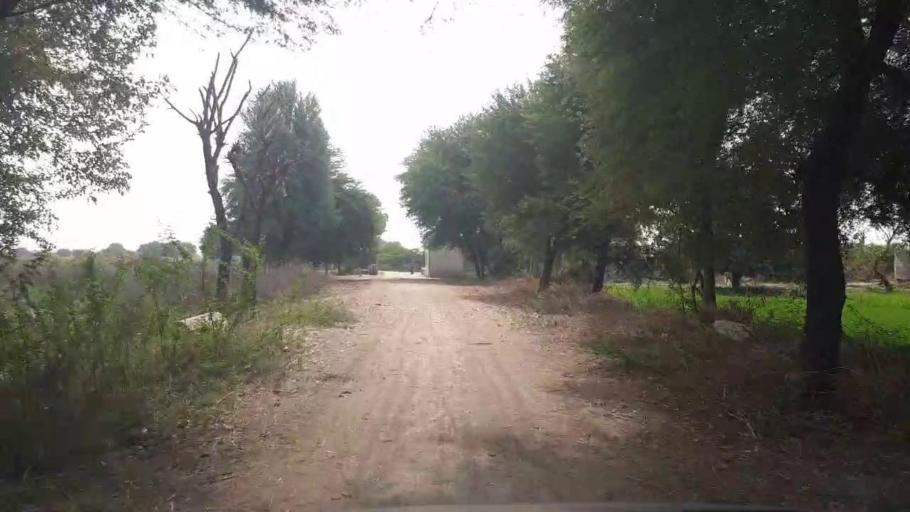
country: PK
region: Sindh
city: Kunri
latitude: 25.2388
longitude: 69.6797
